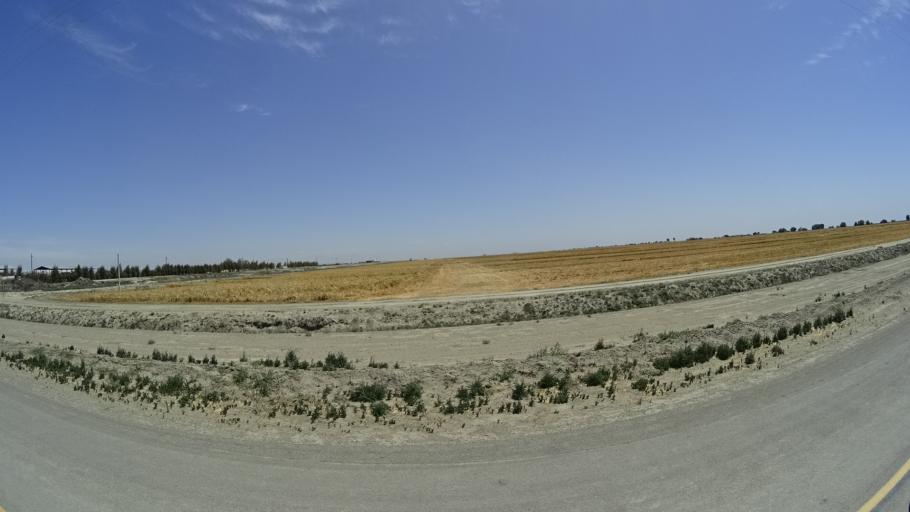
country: US
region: California
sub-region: Kings County
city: Stratford
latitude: 36.1512
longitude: -119.7444
